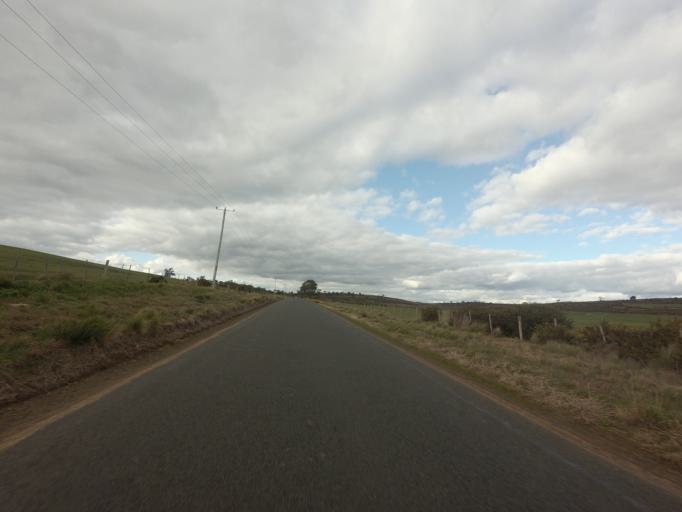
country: AU
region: Tasmania
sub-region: Northern Midlands
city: Evandale
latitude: -41.9029
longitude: 147.3994
